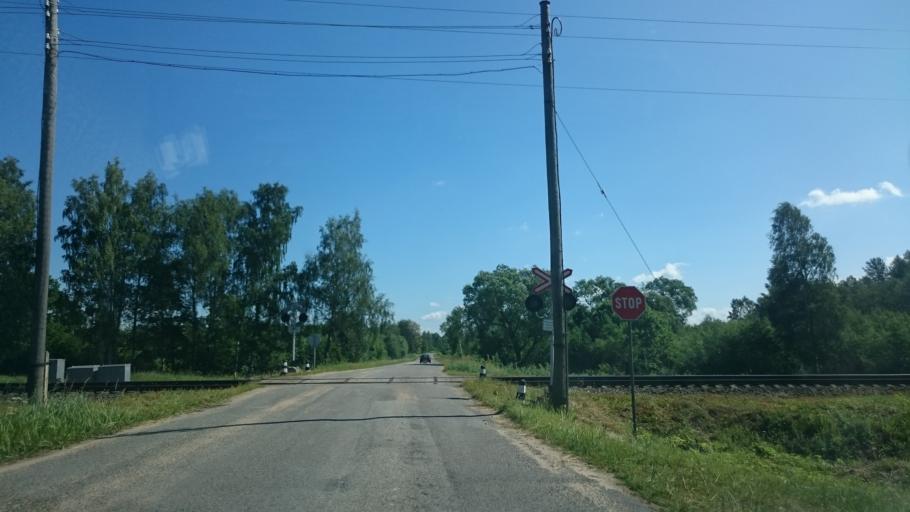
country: LV
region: Ludzas Rajons
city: Ludza
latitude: 56.5108
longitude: 27.7862
